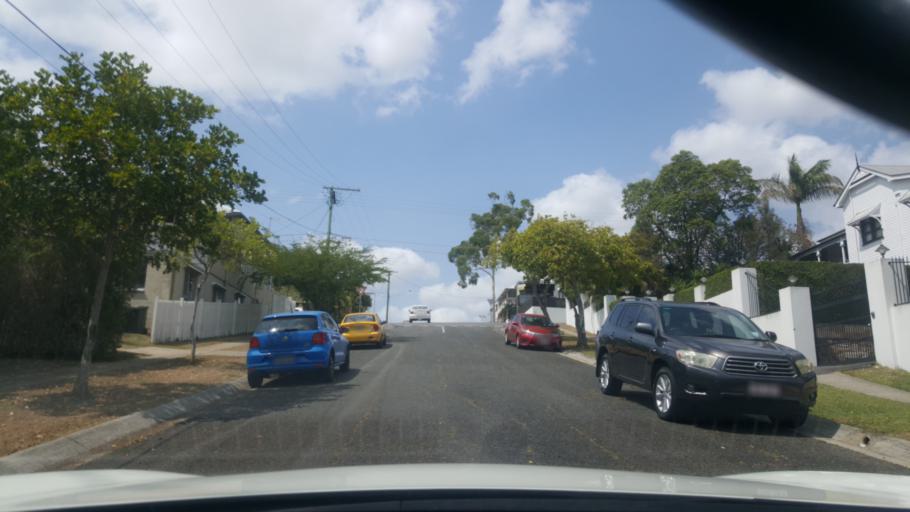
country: AU
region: Queensland
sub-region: Brisbane
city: South Brisbane
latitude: -27.4889
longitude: 153.0220
